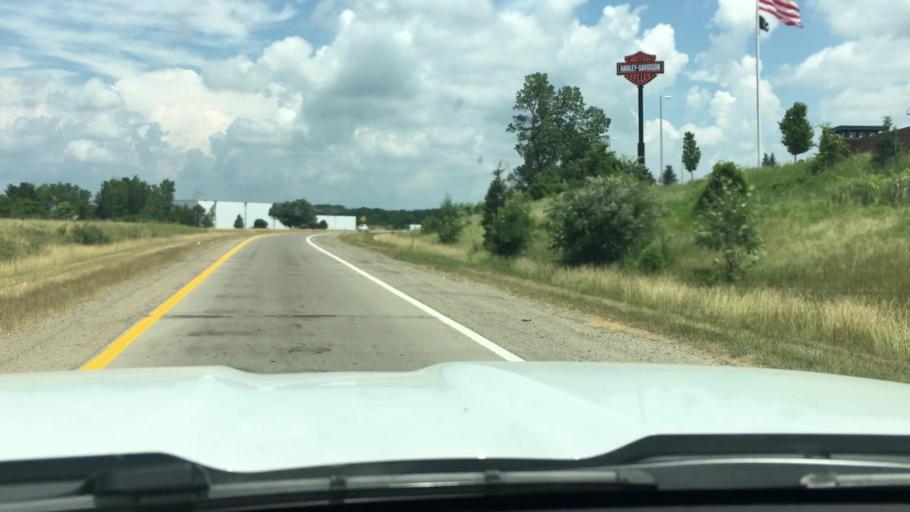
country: US
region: Michigan
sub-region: Ottawa County
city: Hudsonville
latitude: 42.8480
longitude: -85.8587
